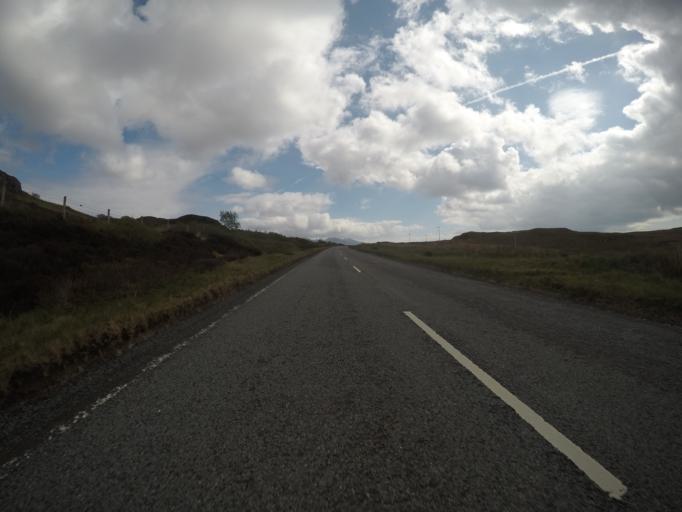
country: GB
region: Scotland
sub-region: Highland
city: Isle of Skye
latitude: 57.3188
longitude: -6.3228
